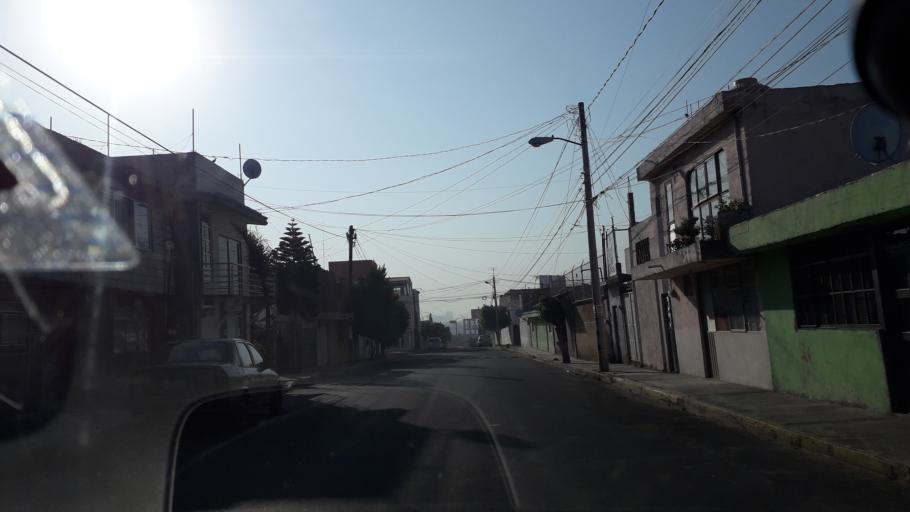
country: MX
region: Puebla
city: Tlazcalancingo
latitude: 19.0364
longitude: -98.2593
